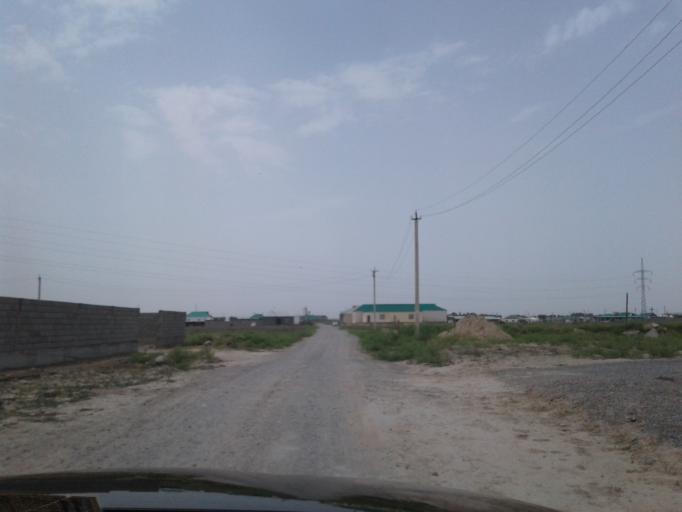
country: TM
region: Ahal
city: Ashgabat
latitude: 37.9806
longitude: 58.3201
